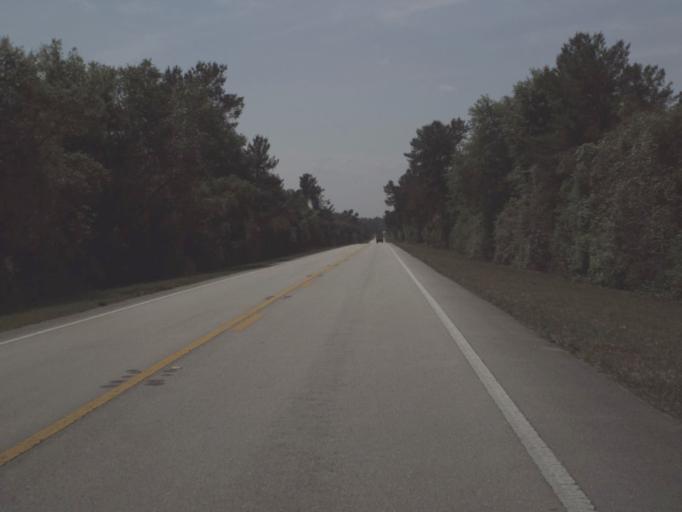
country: US
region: Florida
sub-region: Lake County
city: Astor
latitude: 29.2630
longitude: -81.6465
